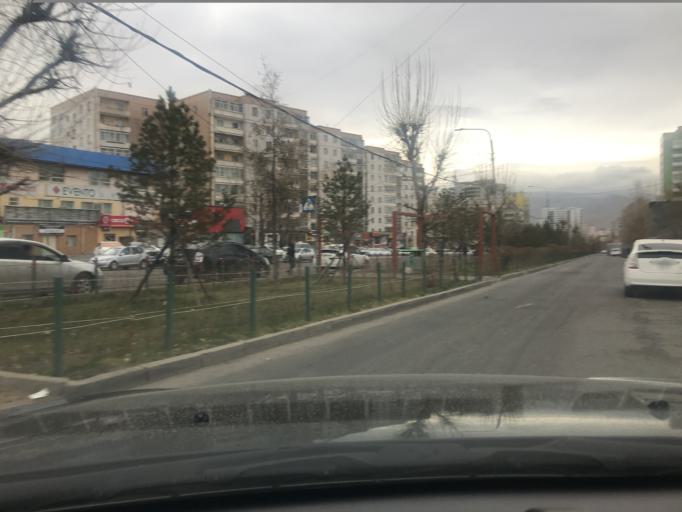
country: MN
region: Ulaanbaatar
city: Ulaanbaatar
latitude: 47.9232
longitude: 106.9419
